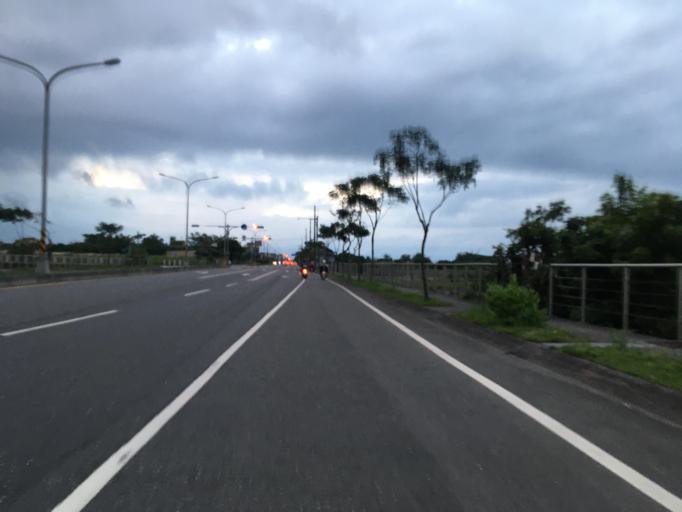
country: TW
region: Taiwan
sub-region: Yilan
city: Yilan
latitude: 24.6168
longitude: 121.8470
